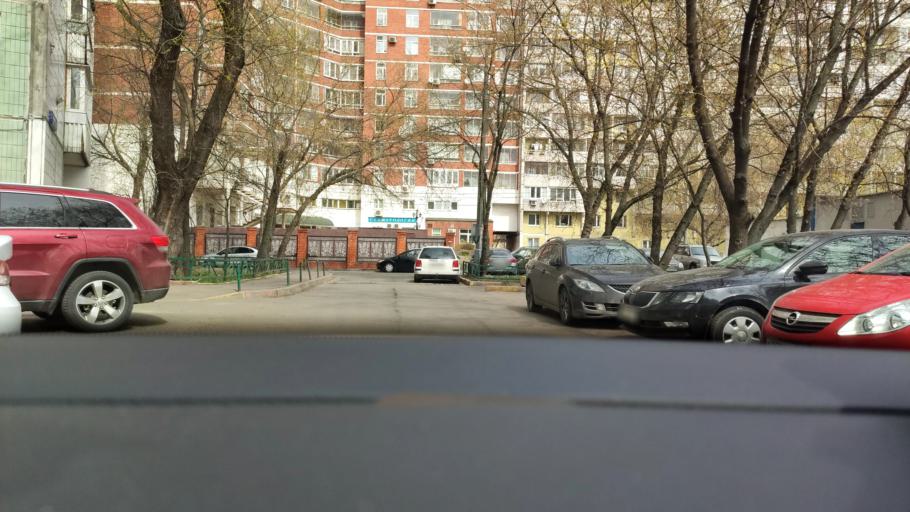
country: RU
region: Moscow
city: Leonovo
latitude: 55.8747
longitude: 37.6612
